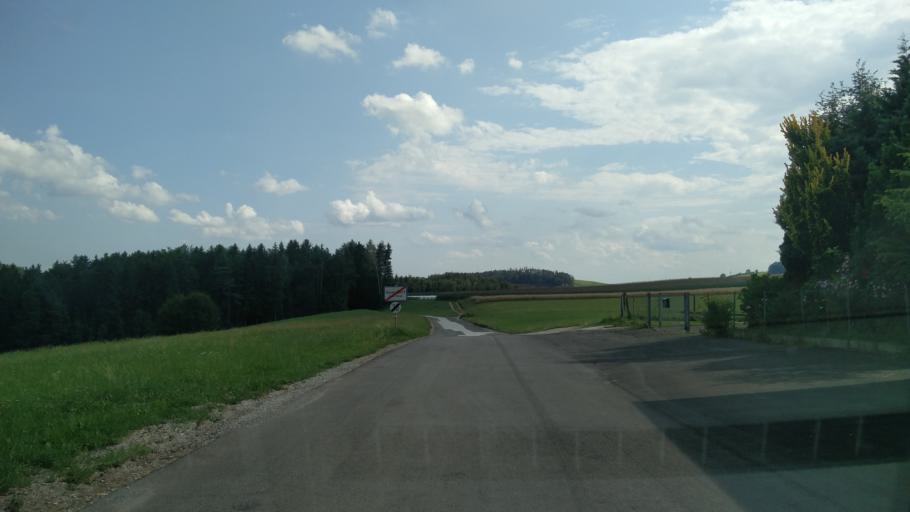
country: AT
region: Styria
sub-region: Politischer Bezirk Weiz
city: Naas
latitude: 47.2451
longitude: 15.6053
